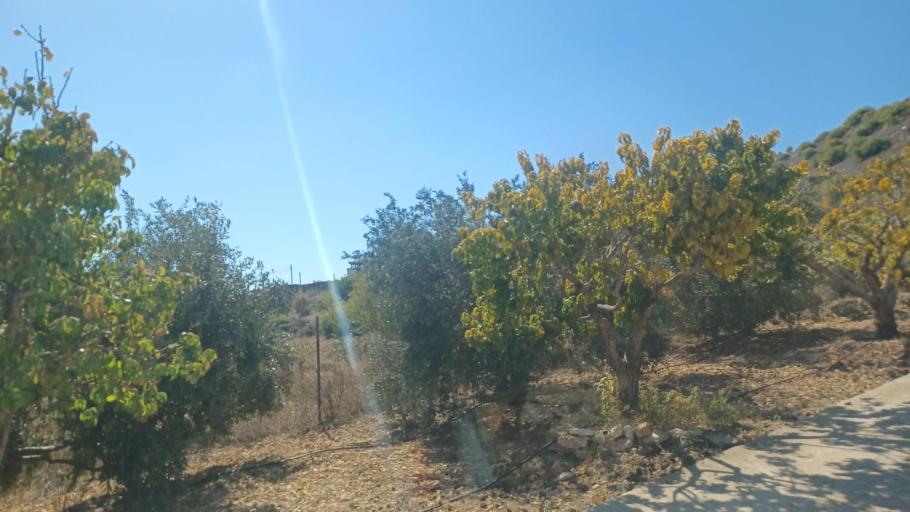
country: CY
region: Pafos
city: Mesogi
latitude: 34.8007
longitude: 32.5152
